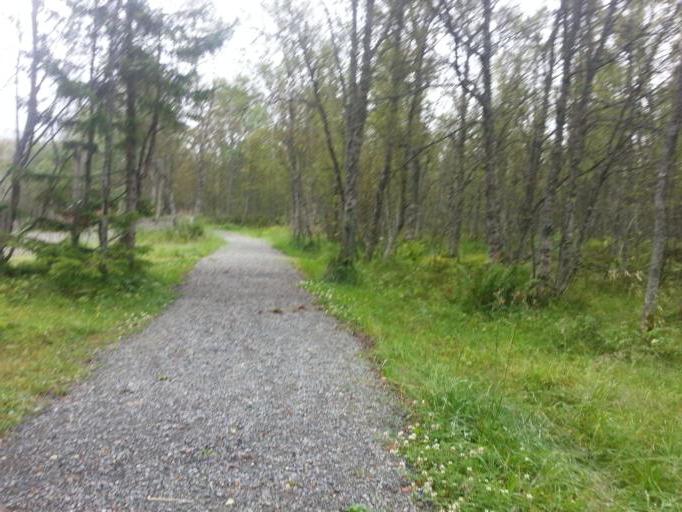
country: NO
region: Troms
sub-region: Tromso
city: Tromso
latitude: 69.6388
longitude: 18.9047
